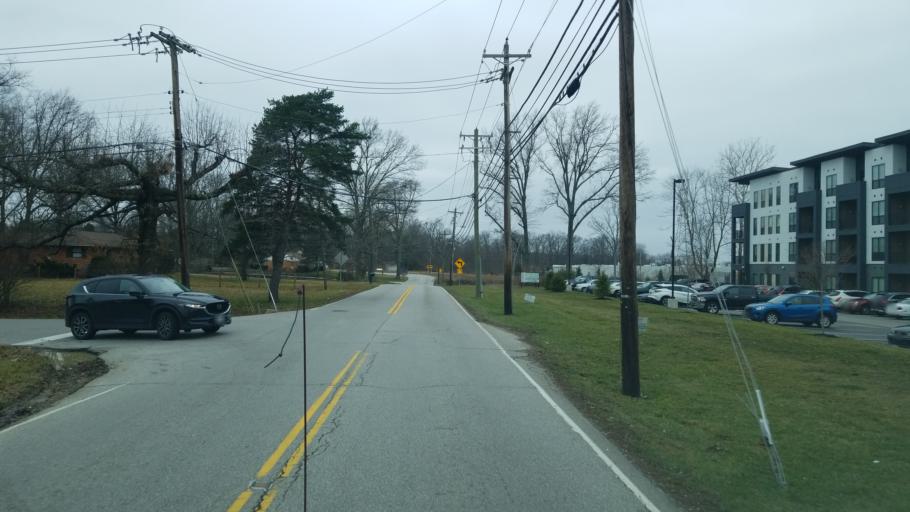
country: US
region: Ohio
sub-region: Clermont County
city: Summerside
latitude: 39.0885
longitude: -84.2652
